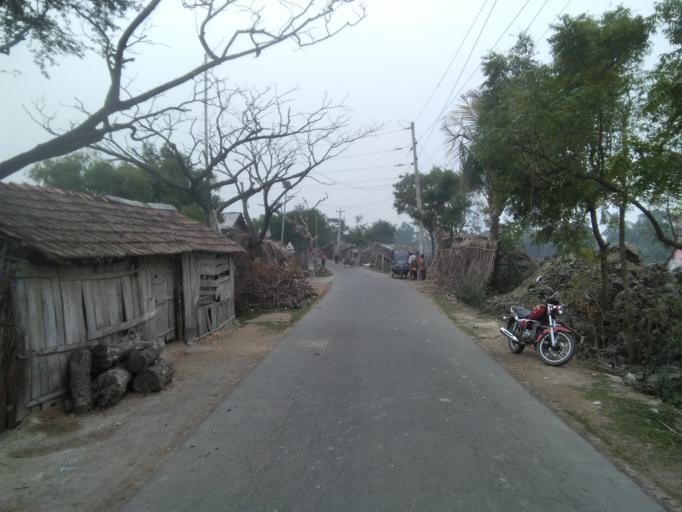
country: BD
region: Khulna
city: Satkhira
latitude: 22.5836
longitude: 89.0668
